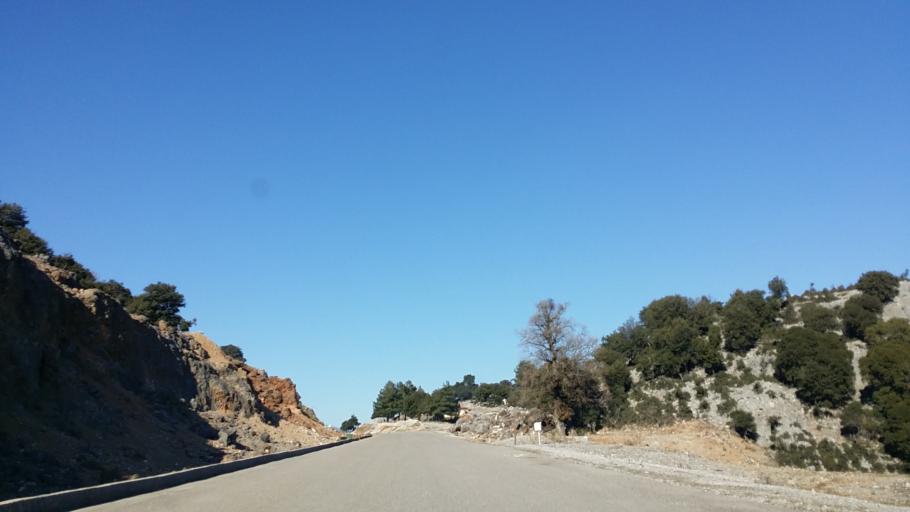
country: GR
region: Central Greece
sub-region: Nomos Evrytanias
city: Kerasochori
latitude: 38.9574
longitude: 21.4658
